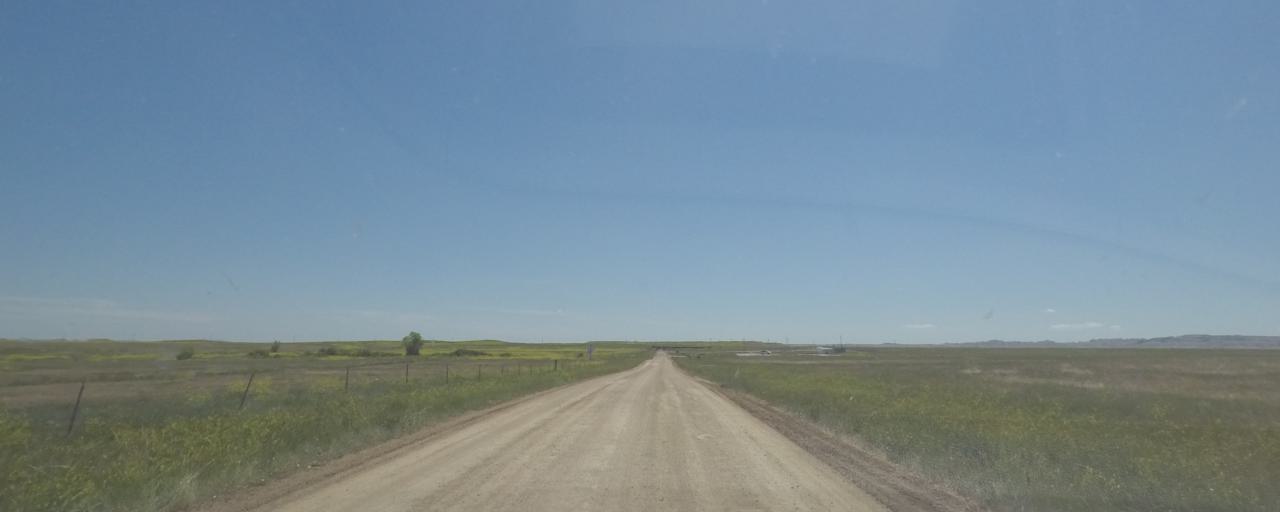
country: US
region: South Dakota
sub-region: Haakon County
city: Philip
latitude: 43.9356
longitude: -102.1587
